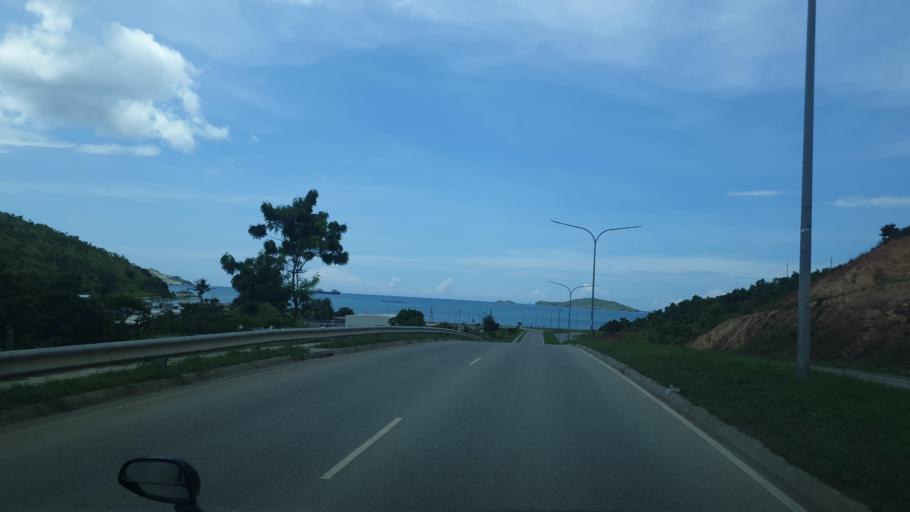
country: PG
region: National Capital
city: Port Moresby
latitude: -9.4348
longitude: 147.1397
